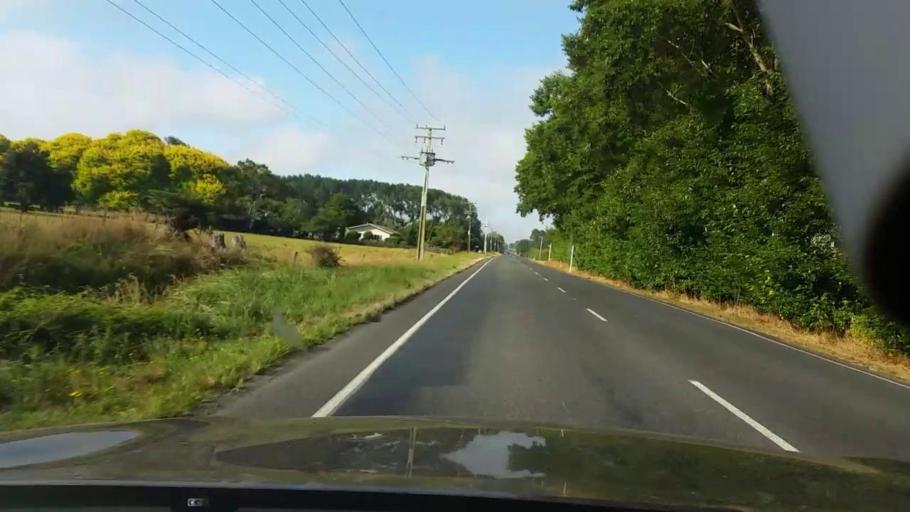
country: NZ
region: Waikato
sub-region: Hamilton City
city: Hamilton
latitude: -37.5993
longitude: 175.3534
